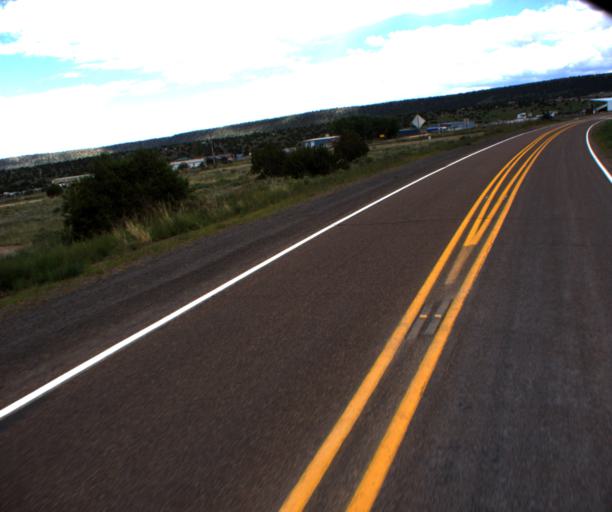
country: US
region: Arizona
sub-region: Apache County
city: Eagar
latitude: 34.1106
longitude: -109.2534
